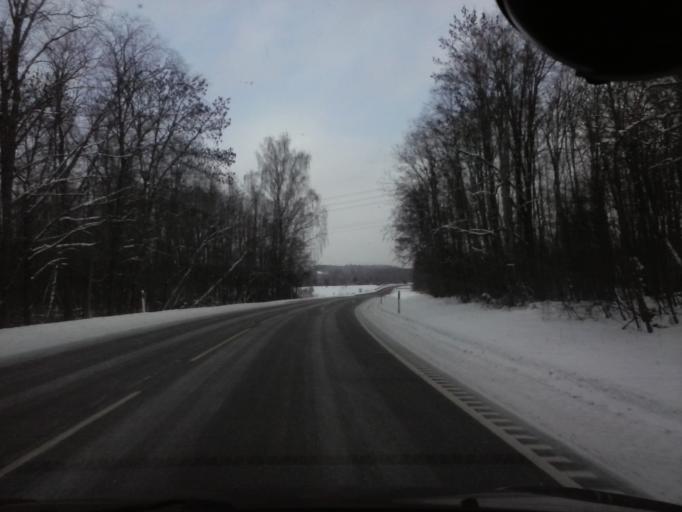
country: EE
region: Viljandimaa
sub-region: Viljandi linn
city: Viljandi
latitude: 58.3532
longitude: 25.4552
